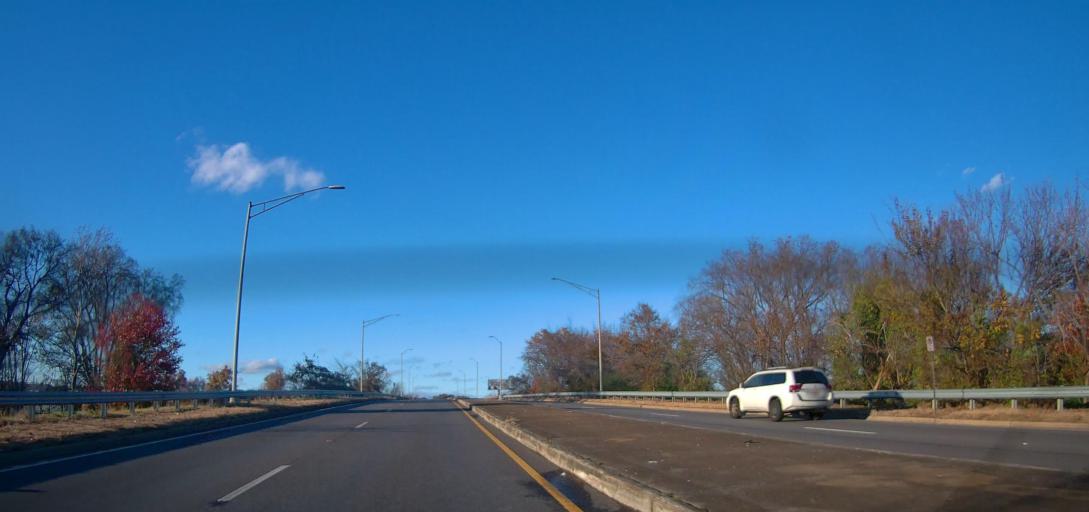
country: US
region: Alabama
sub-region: Jefferson County
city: Birmingham
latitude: 33.5474
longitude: -86.8162
